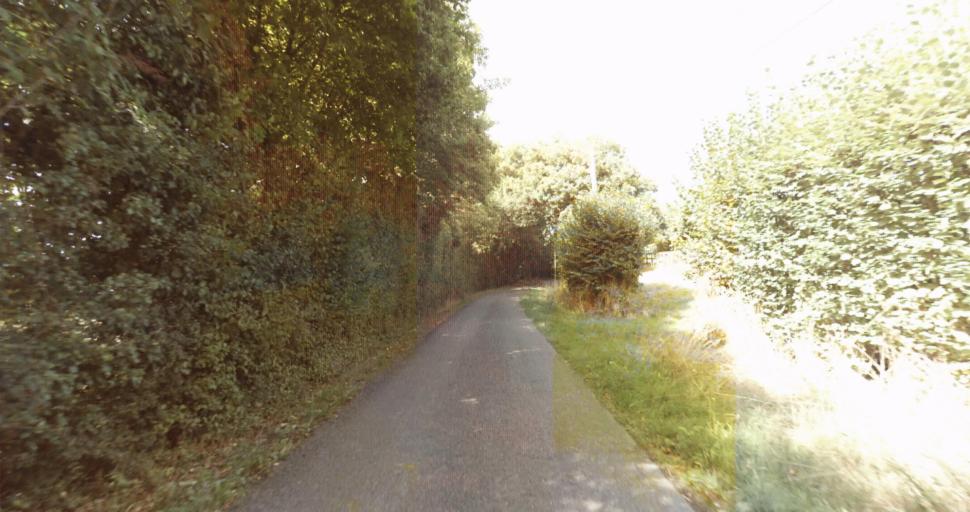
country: FR
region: Lower Normandy
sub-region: Departement de l'Orne
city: Sees
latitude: 48.7142
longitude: 0.1742
